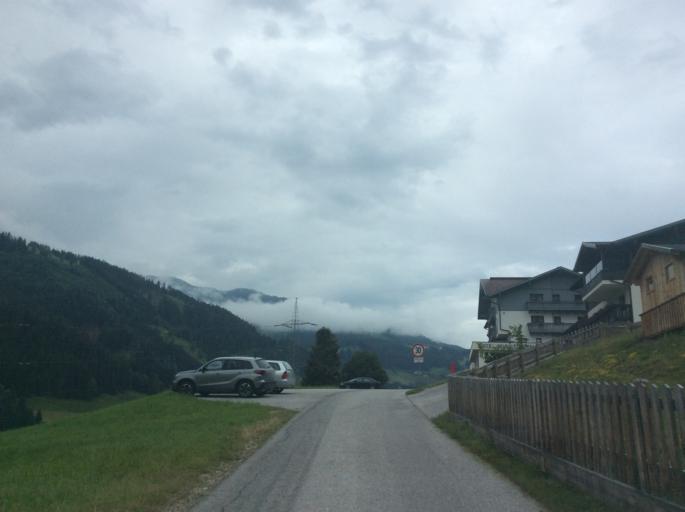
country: AT
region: Styria
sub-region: Politischer Bezirk Liezen
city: Schladming
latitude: 47.3914
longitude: 13.6396
